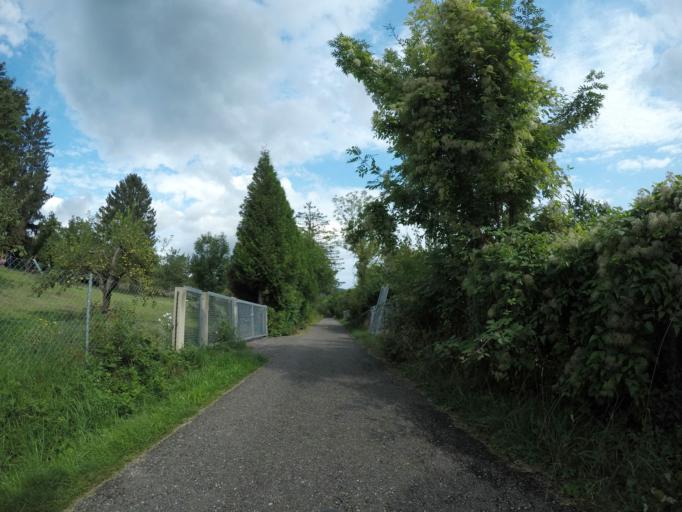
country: DE
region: Baden-Wuerttemberg
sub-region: Tuebingen Region
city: Eningen unter Achalm
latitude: 48.4797
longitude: 9.2427
